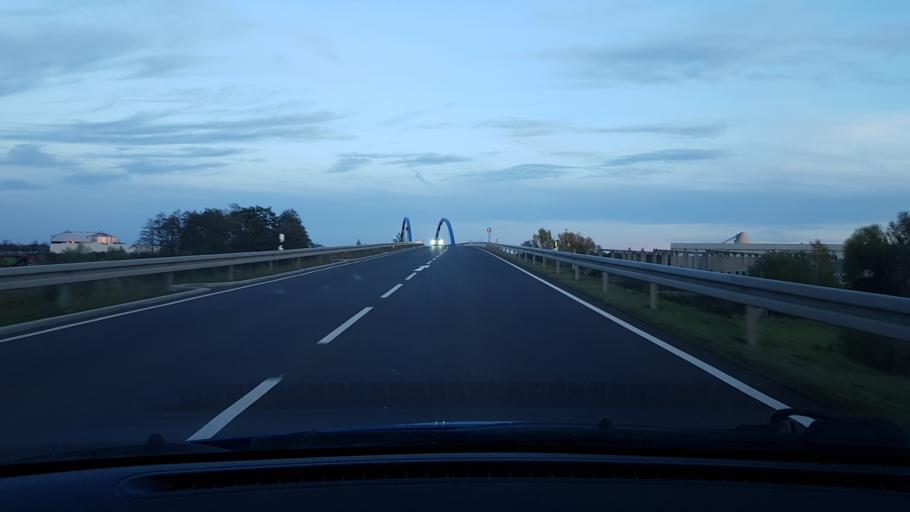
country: DE
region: Saxony-Anhalt
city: Gommern
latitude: 52.0862
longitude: 11.8163
